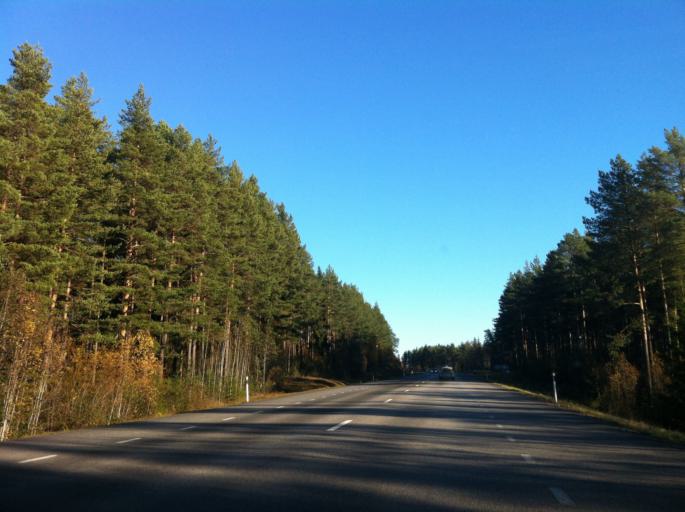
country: SE
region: Dalarna
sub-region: Rattviks Kommun
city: Vikarbyn
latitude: 60.9062
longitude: 14.9742
